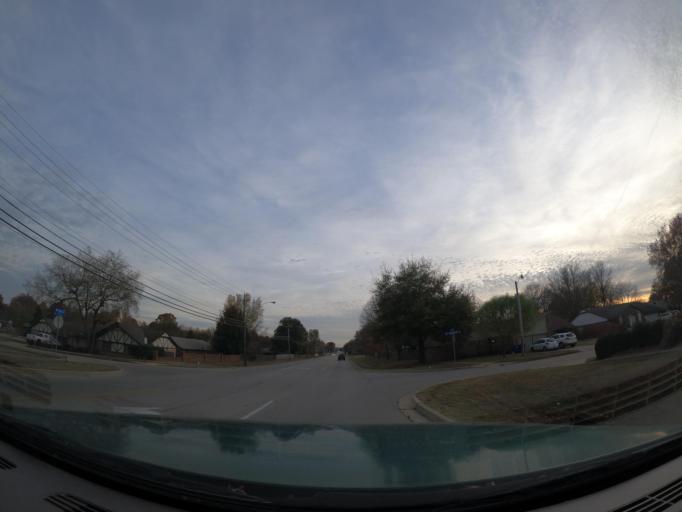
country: US
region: Oklahoma
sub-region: Tulsa County
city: Broken Arrow
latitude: 35.9845
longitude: -95.7974
